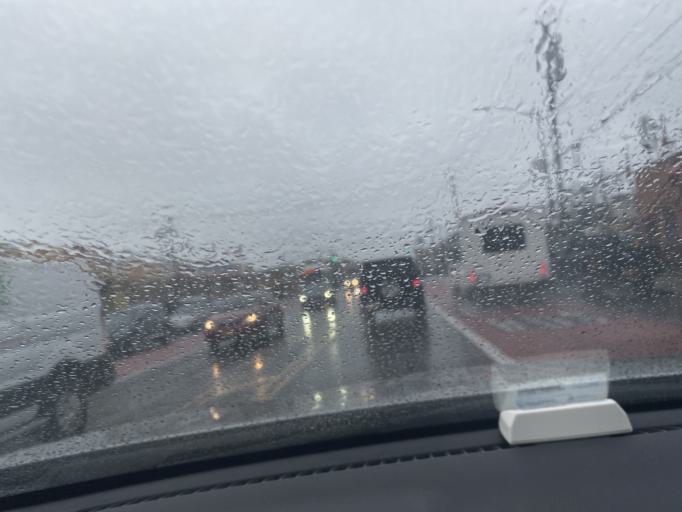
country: US
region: New York
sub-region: Kings County
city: Brooklyn
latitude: 40.6475
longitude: -73.9299
